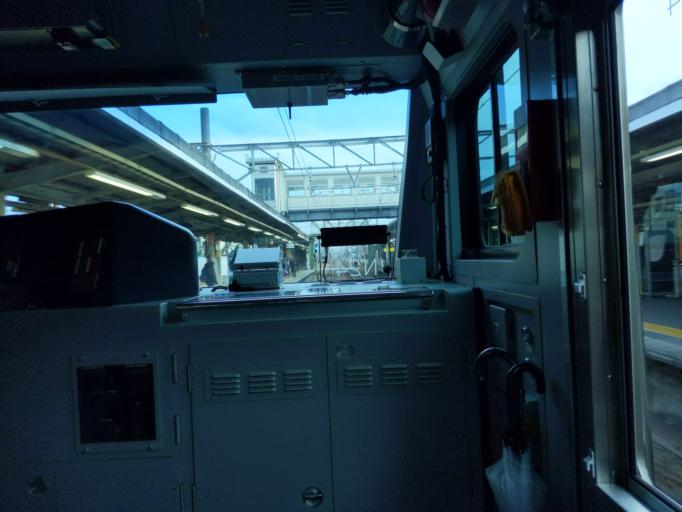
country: JP
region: Kanagawa
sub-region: Kawasaki-shi
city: Kawasaki
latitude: 35.5395
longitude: 139.6804
